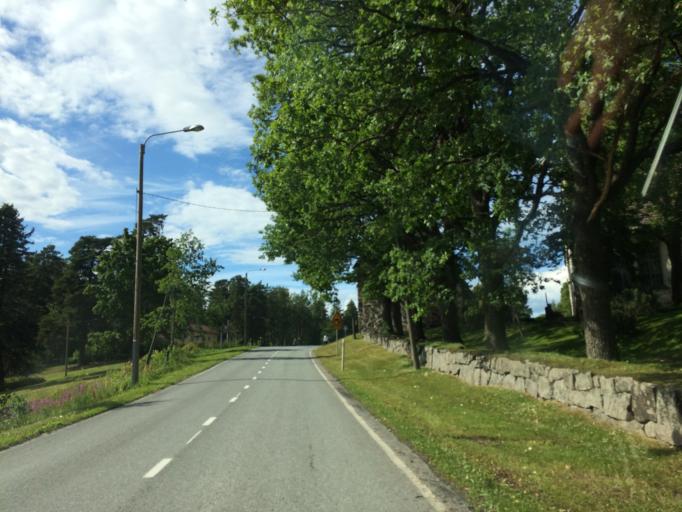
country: FI
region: Haeme
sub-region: Haemeenlinna
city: Janakkala
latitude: 60.8929
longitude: 24.5954
